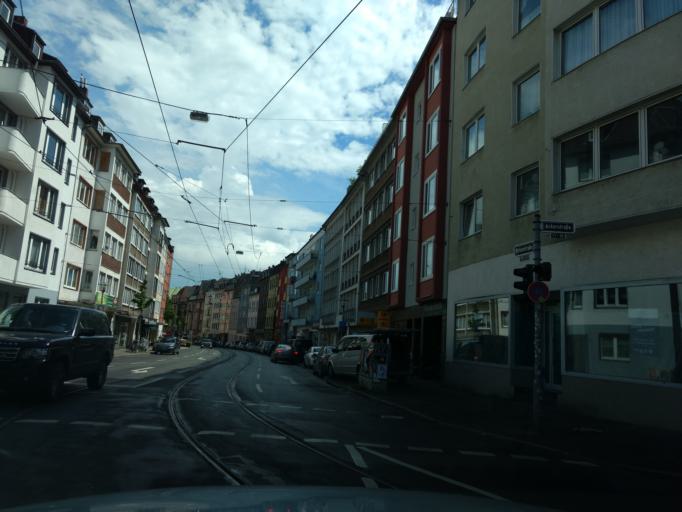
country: DE
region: North Rhine-Westphalia
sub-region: Regierungsbezirk Dusseldorf
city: Dusseldorf
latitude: 51.2276
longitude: 6.8015
